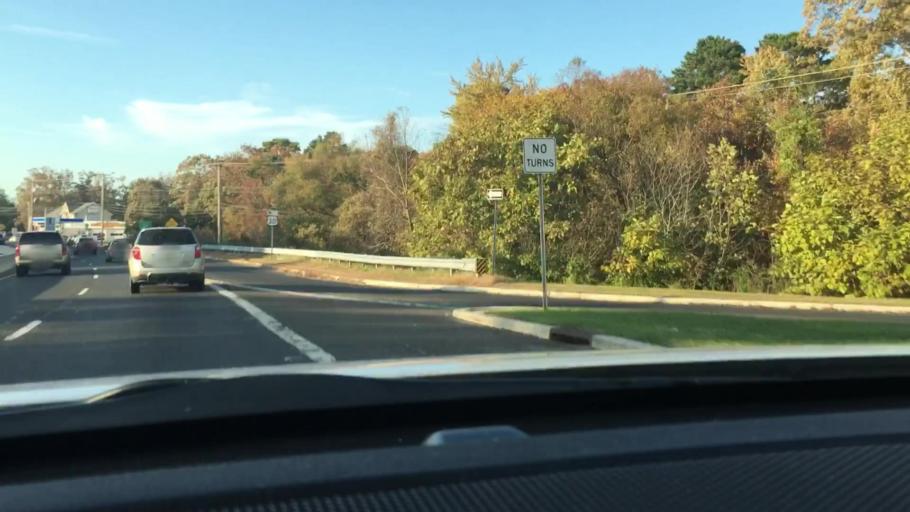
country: US
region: New Jersey
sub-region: Atlantic County
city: Absecon
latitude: 39.4385
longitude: -74.5179
